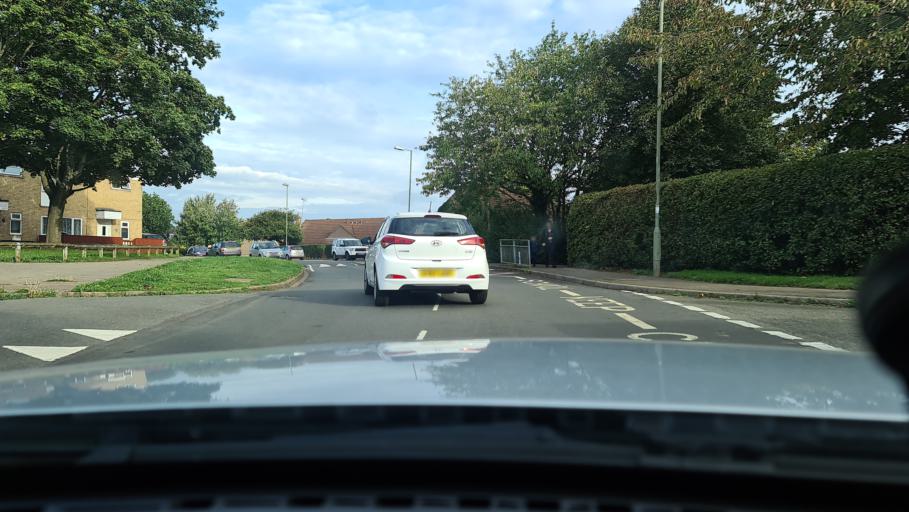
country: GB
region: England
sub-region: Oxfordshire
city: Banbury
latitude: 52.0668
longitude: -1.3652
